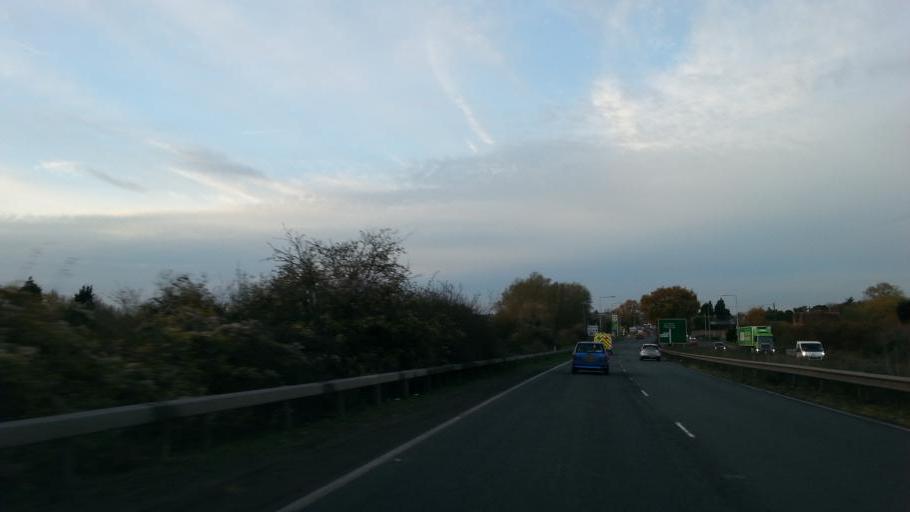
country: GB
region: England
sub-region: Central Bedfordshire
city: Astwick
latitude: 52.0259
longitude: -0.2126
